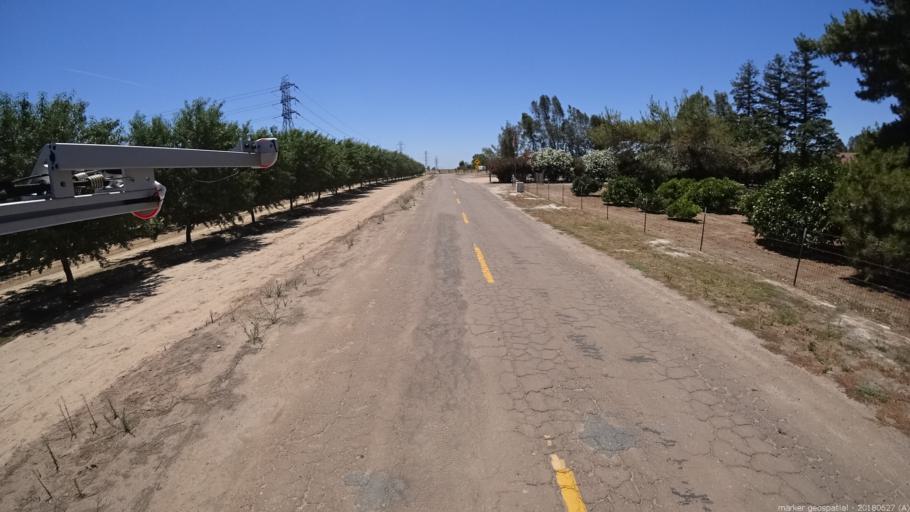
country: US
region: California
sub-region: Madera County
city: Bonadelle Ranchos-Madera Ranchos
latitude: 36.9334
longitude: -119.8580
